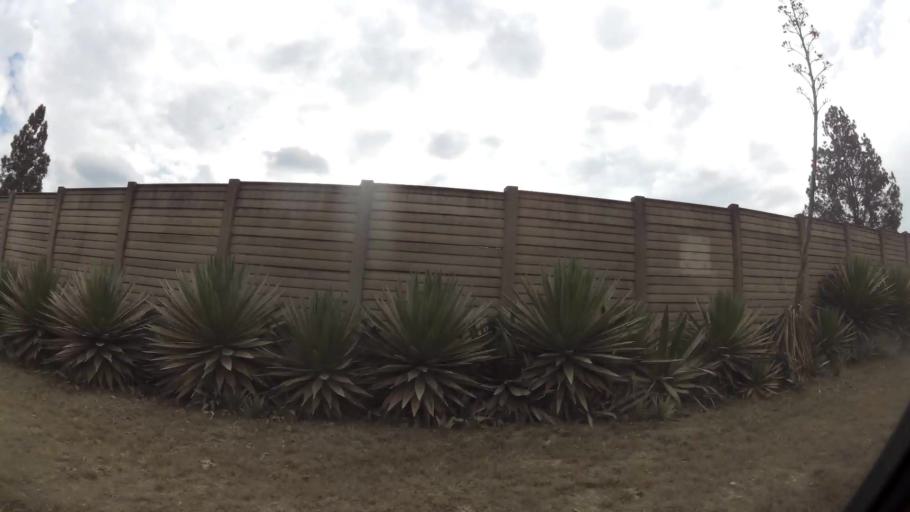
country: ZA
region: Gauteng
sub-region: West Rand District Municipality
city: Muldersdriseloop
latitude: -26.0672
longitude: 27.8890
